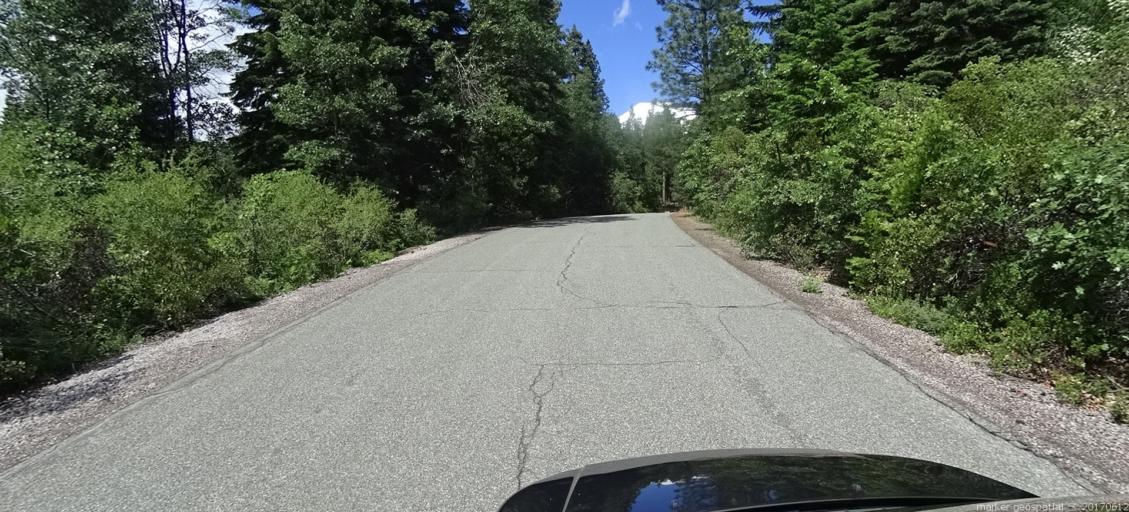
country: US
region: California
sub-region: Siskiyou County
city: Mount Shasta
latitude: 41.3028
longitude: -122.2898
